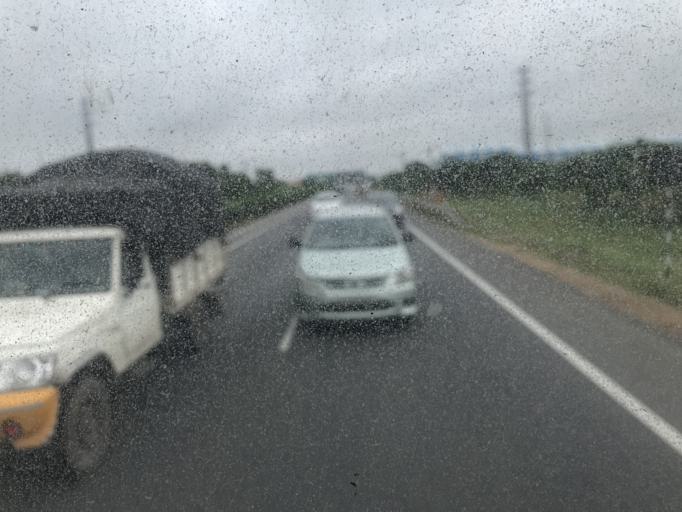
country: IN
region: Telangana
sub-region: Mahbubnagar
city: Farrukhnagar
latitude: 17.0243
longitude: 78.1979
